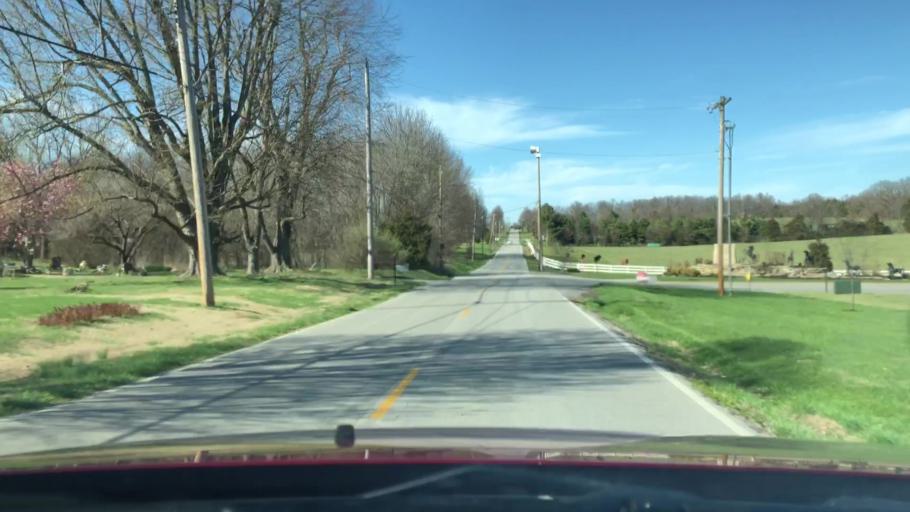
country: US
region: Missouri
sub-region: Greene County
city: Strafford
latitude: 37.2314
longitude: -93.1884
